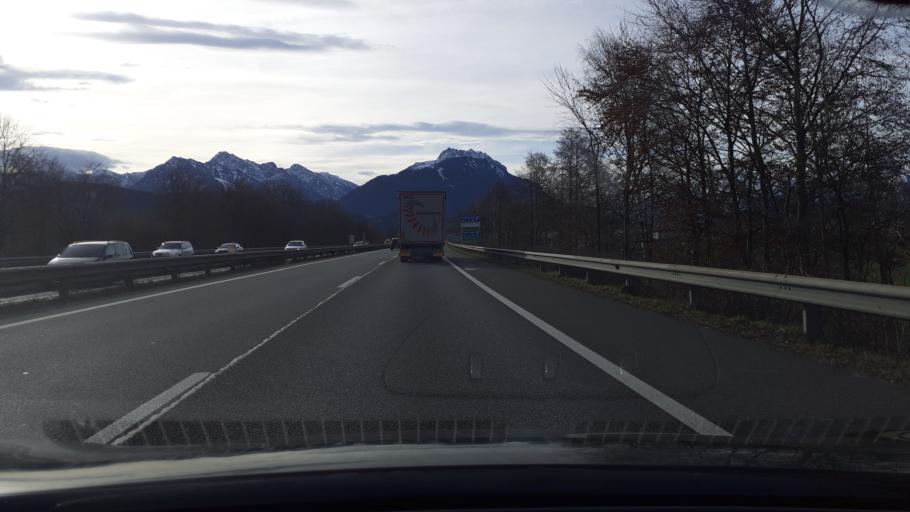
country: AT
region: Vorarlberg
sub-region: Politischer Bezirk Feldkirch
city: Rankweil
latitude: 47.2856
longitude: 9.6255
